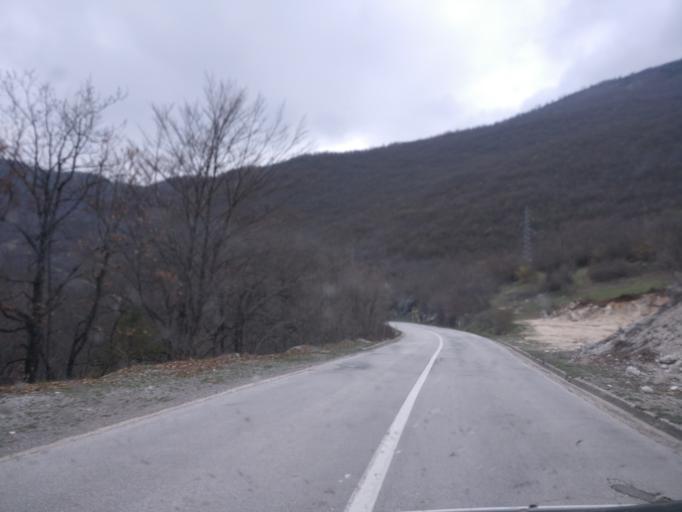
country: ME
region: Opstina Pluzine
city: Pluzine
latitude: 43.1094
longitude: 18.8150
